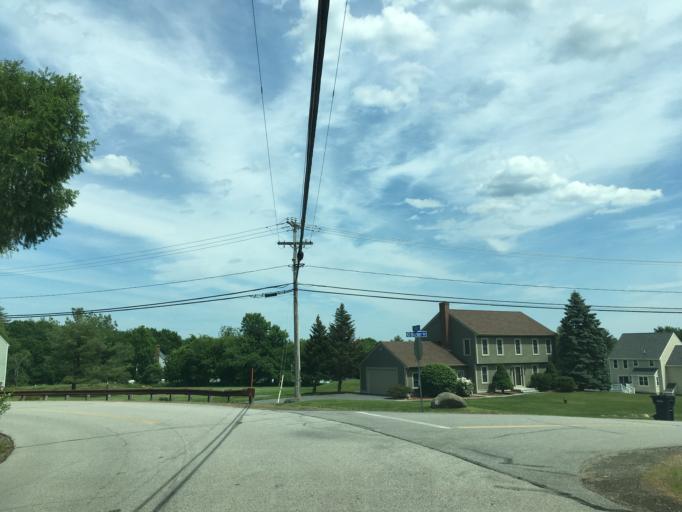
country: US
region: New Hampshire
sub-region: Rockingham County
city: Stratham Station
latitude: 43.0224
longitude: -70.8763
